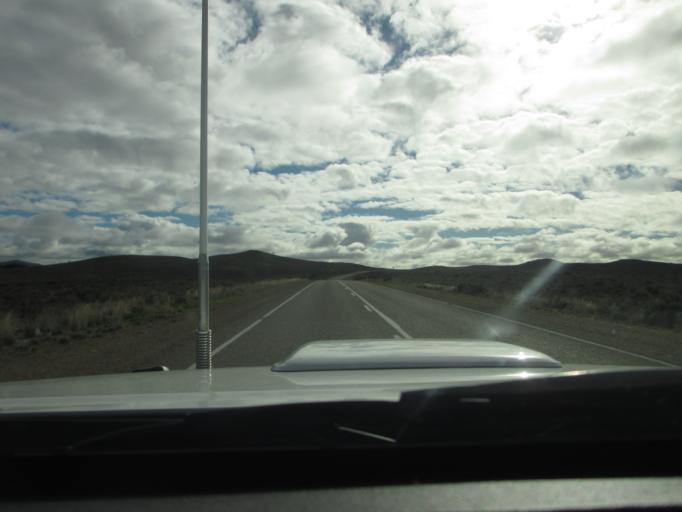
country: AU
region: South Australia
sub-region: Flinders Ranges
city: Quorn
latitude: -32.2777
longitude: 138.4954
